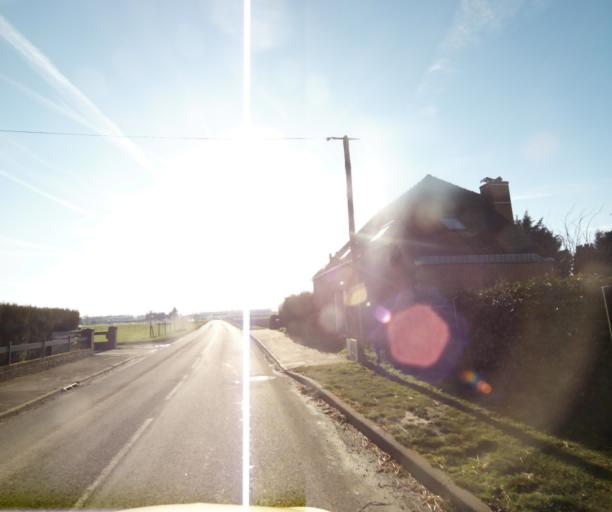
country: FR
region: Nord-Pas-de-Calais
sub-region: Departement du Nord
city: Saultain
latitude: 50.3456
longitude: 3.5895
